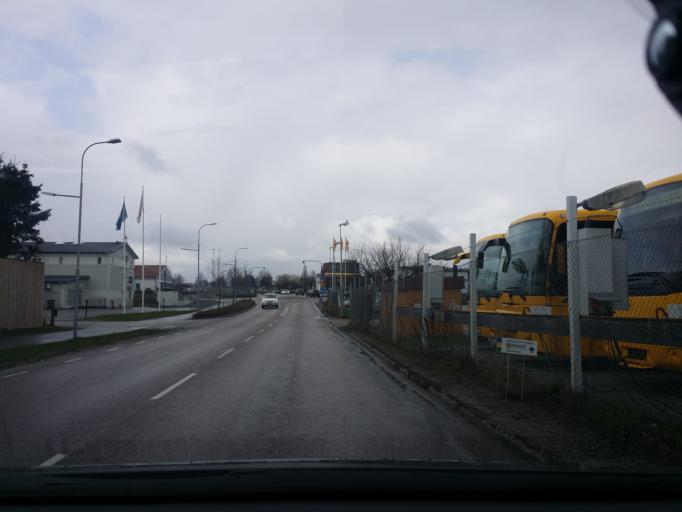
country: SE
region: Uppsala
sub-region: Enkopings Kommun
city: Enkoping
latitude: 59.6473
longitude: 17.0890
